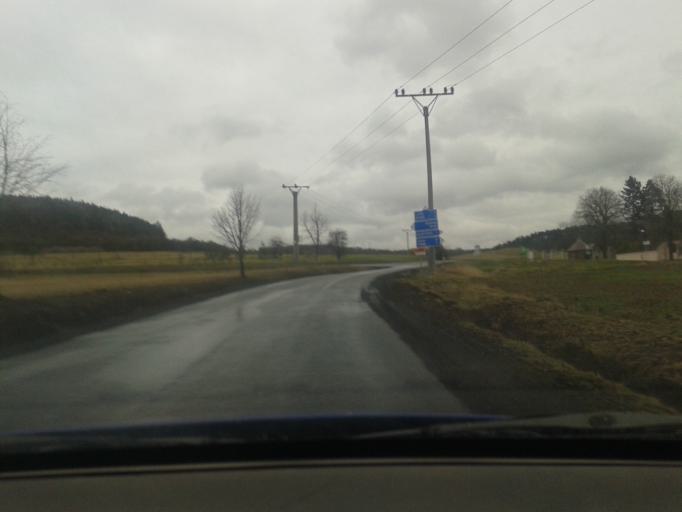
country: CZ
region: Central Bohemia
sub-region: Okres Beroun
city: Beroun
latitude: 49.9261
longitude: 14.0707
